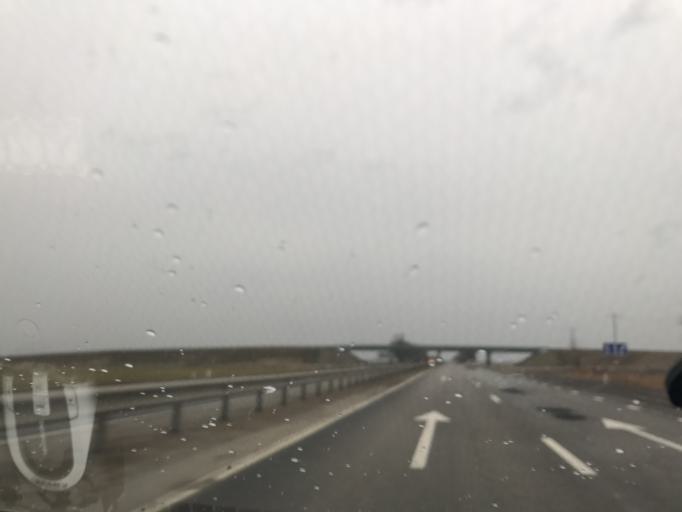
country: RU
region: Krasnodarskiy
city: Pavlovskaya
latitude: 46.1606
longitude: 39.8442
